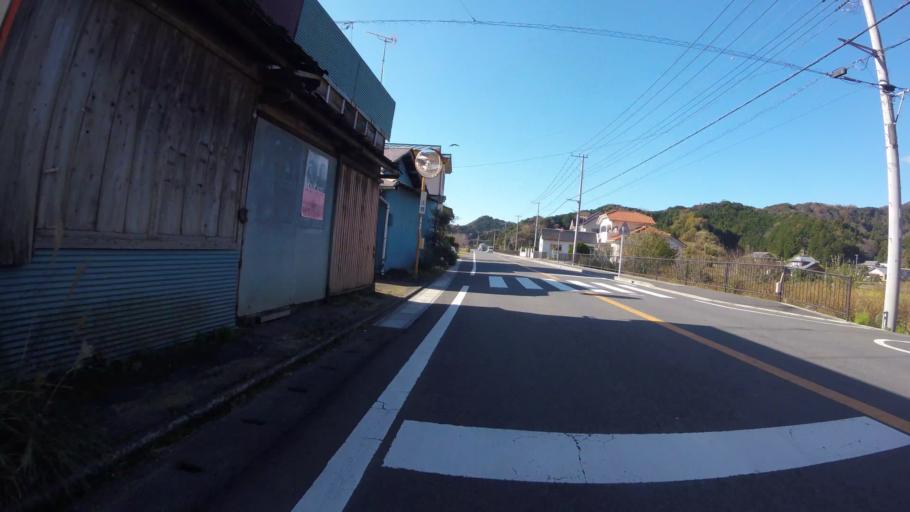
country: JP
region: Shizuoka
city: Shimoda
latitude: 34.7571
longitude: 138.8099
